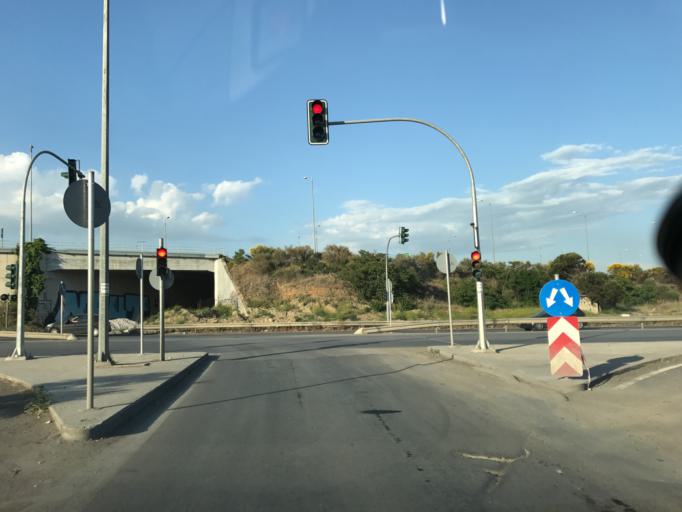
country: GR
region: Central Macedonia
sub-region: Nomos Thessalonikis
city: Menemeni
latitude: 40.6522
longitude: 22.9004
